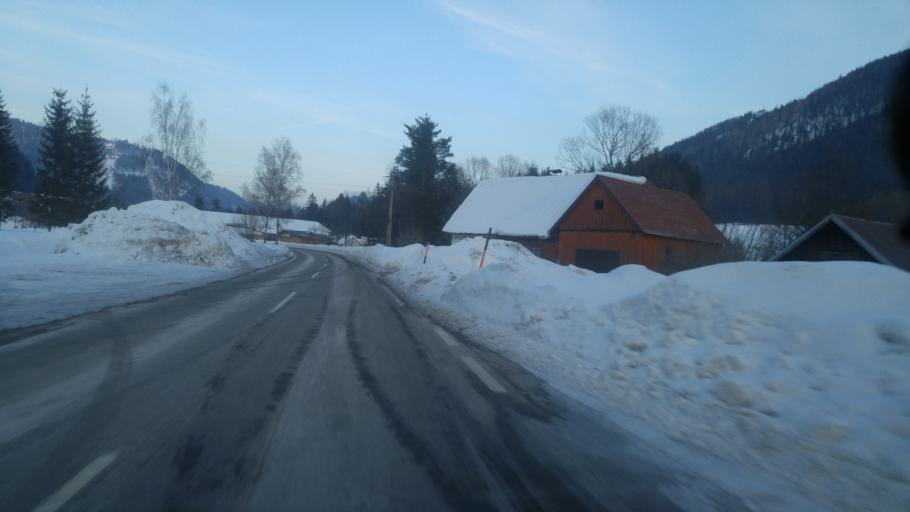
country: AT
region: Lower Austria
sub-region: Politischer Bezirk Wiener Neustadt
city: Rohr im Gebirge
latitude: 47.8806
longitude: 15.7102
